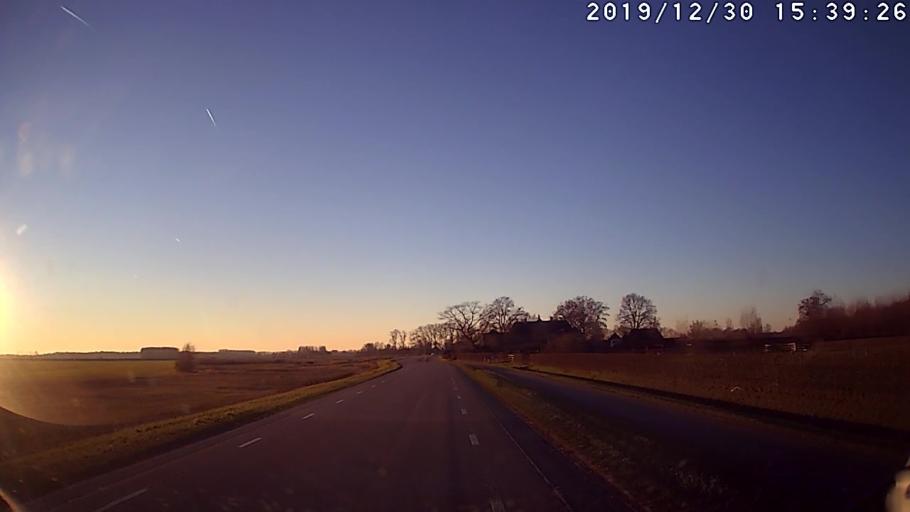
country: NL
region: Overijssel
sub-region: Gemeente Raalte
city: Heino
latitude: 52.4604
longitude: 6.1612
